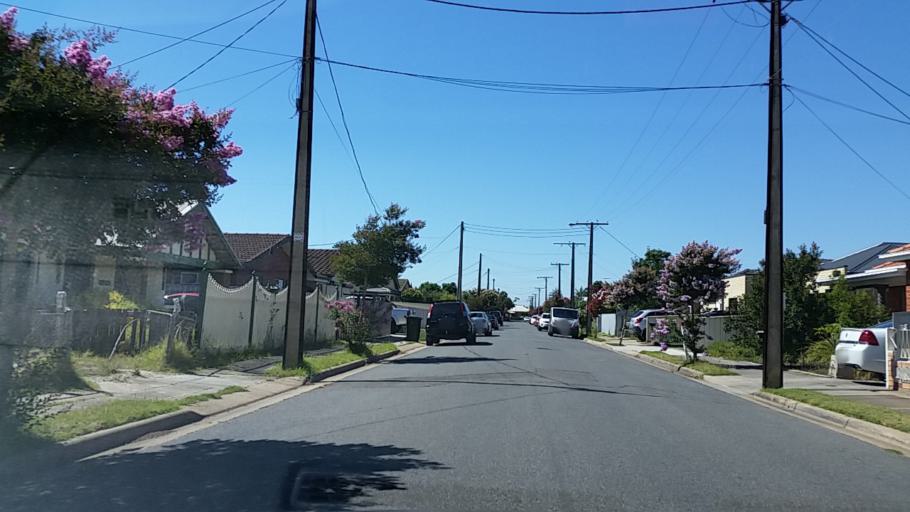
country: AU
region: South Australia
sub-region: Charles Sturt
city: Albert Park
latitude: -34.8714
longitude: 138.5158
